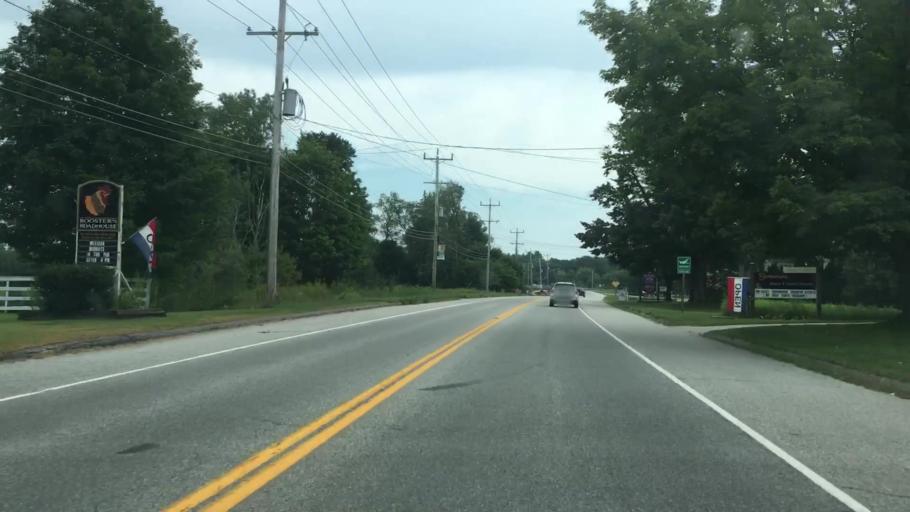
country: US
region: Maine
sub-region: Oxford County
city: Bethel
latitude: 44.4212
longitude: -70.7974
